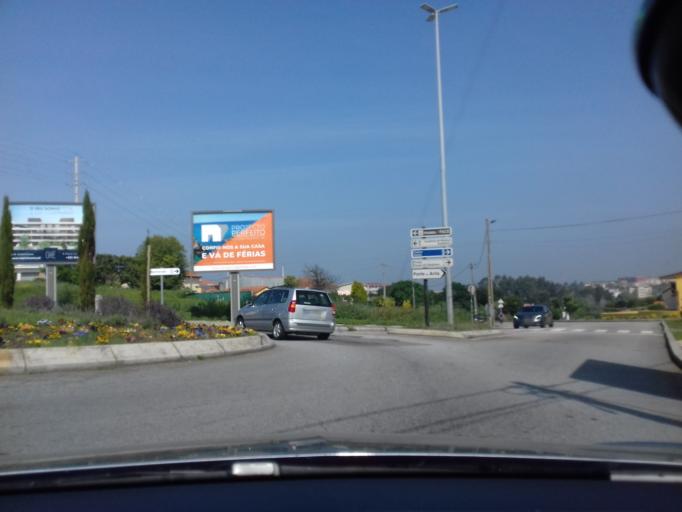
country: PT
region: Aveiro
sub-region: Espinho
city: Silvalde
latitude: 41.0085
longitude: -8.6245
